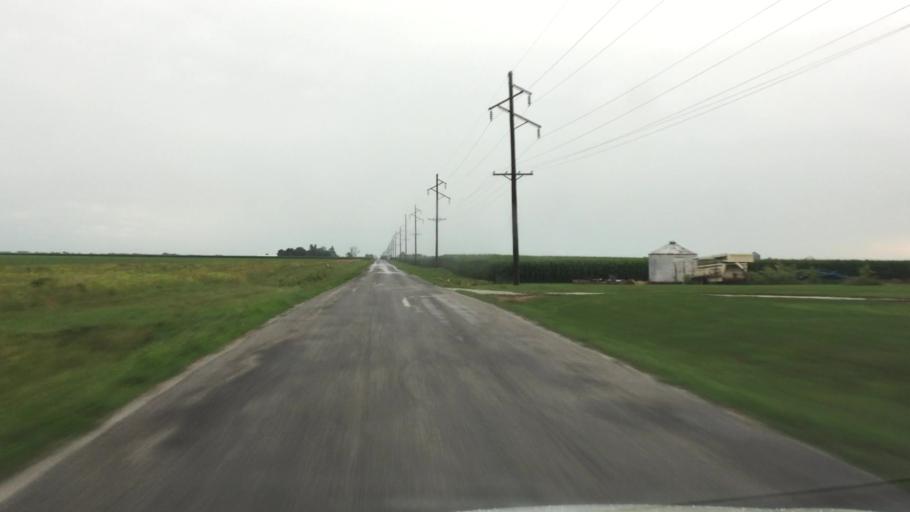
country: US
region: Illinois
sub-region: Hancock County
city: Nauvoo
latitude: 40.5181
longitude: -91.2692
